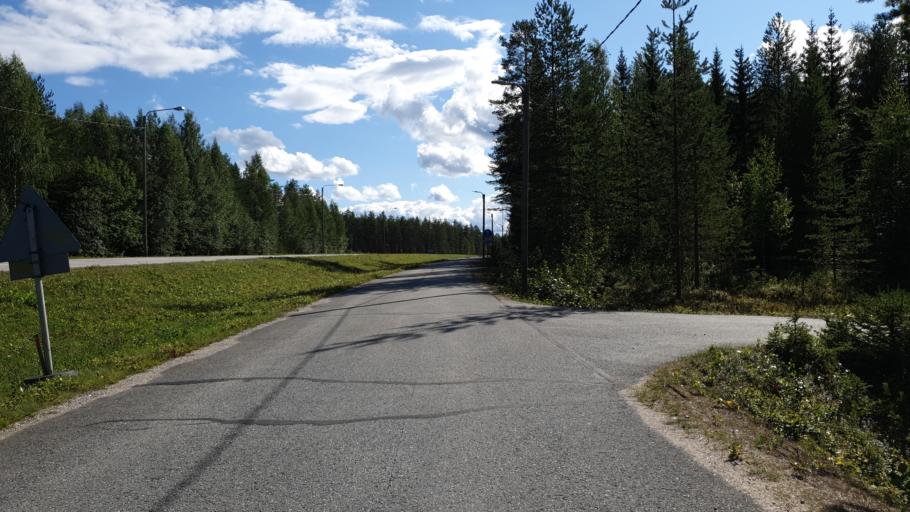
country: FI
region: Kainuu
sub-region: Kehys-Kainuu
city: Kuhmo
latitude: 64.1016
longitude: 29.4751
